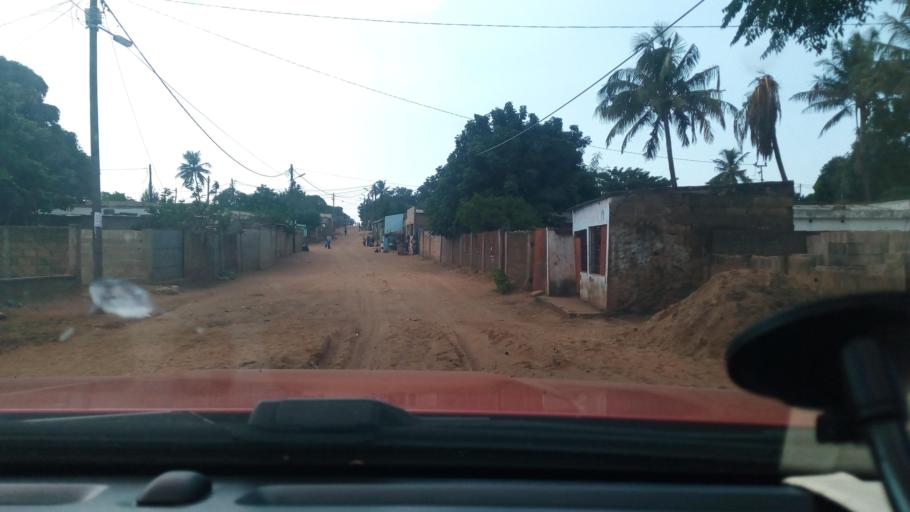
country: MZ
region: Maputo City
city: Maputo
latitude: -25.9208
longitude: 32.5971
